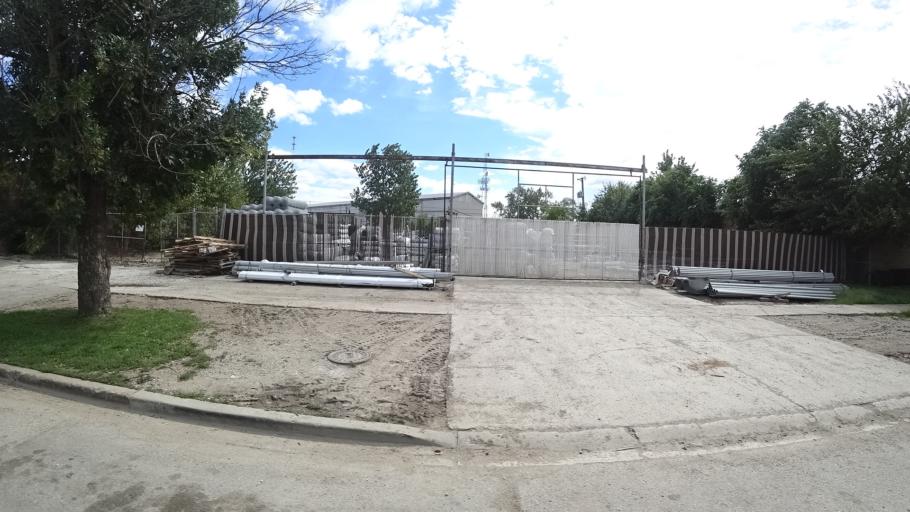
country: US
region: Illinois
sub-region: Cook County
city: Chicago Ridge
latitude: 41.7121
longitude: -87.7864
